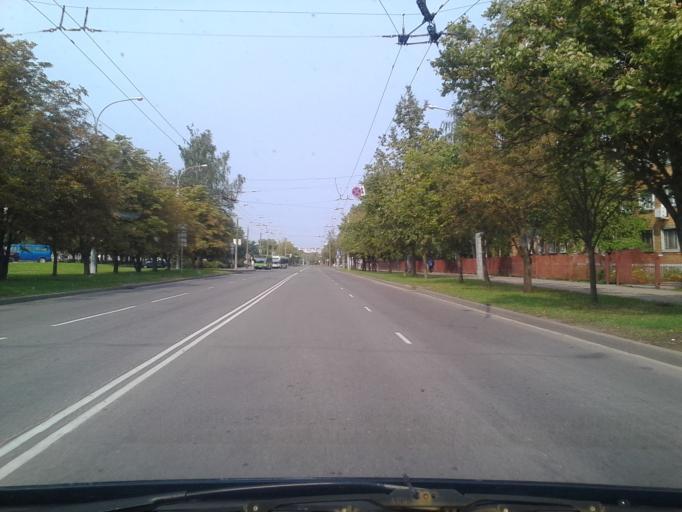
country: BY
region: Minsk
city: Syenitsa
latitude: 53.8587
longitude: 27.4979
